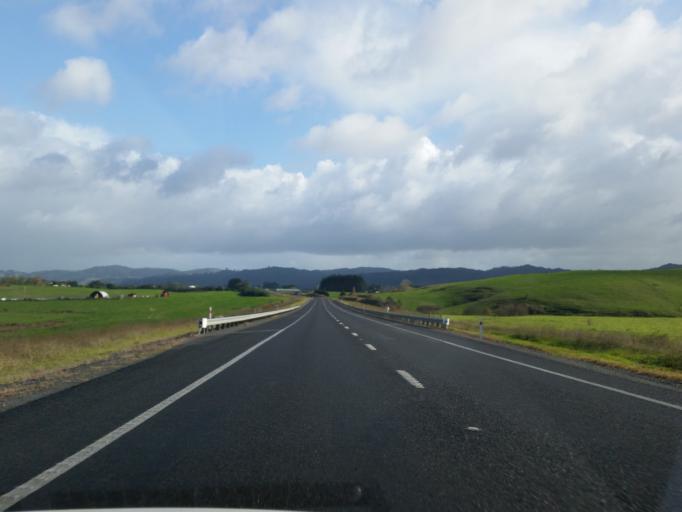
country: NZ
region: Waikato
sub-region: Waikato District
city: Te Kauwhata
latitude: -37.2248
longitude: 175.1497
